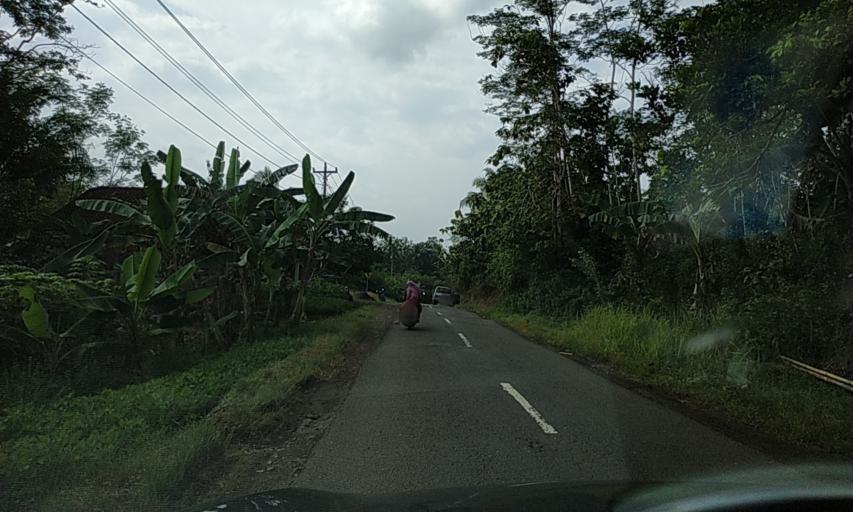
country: ID
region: Central Java
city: Meluwung
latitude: -7.3846
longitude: 108.6987
